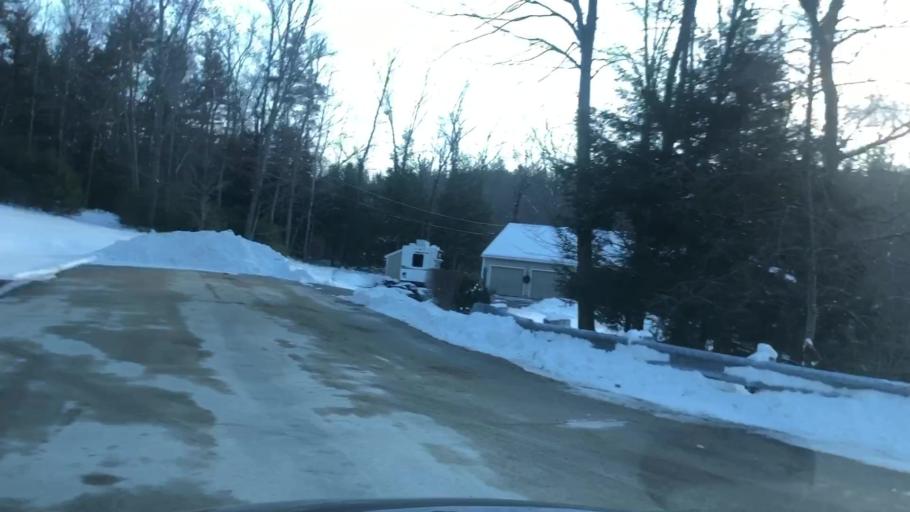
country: US
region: New Hampshire
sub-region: Hillsborough County
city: Milford
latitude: 42.8147
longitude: -71.6702
